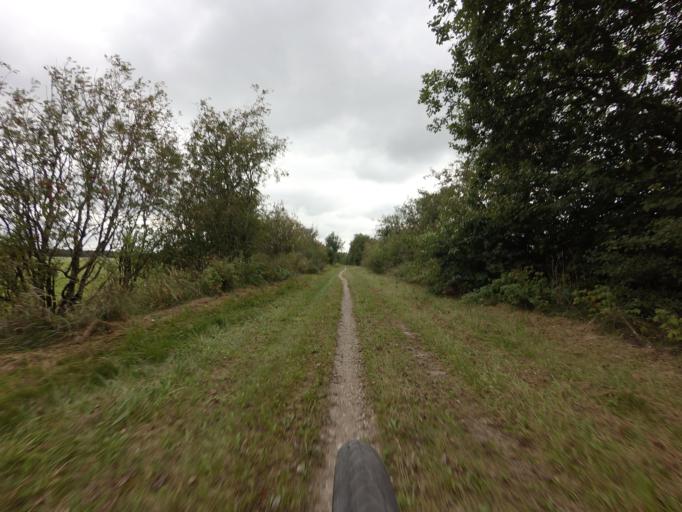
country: DK
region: Central Jutland
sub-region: Ikast-Brande Kommune
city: Brande
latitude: 55.8612
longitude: 9.0227
